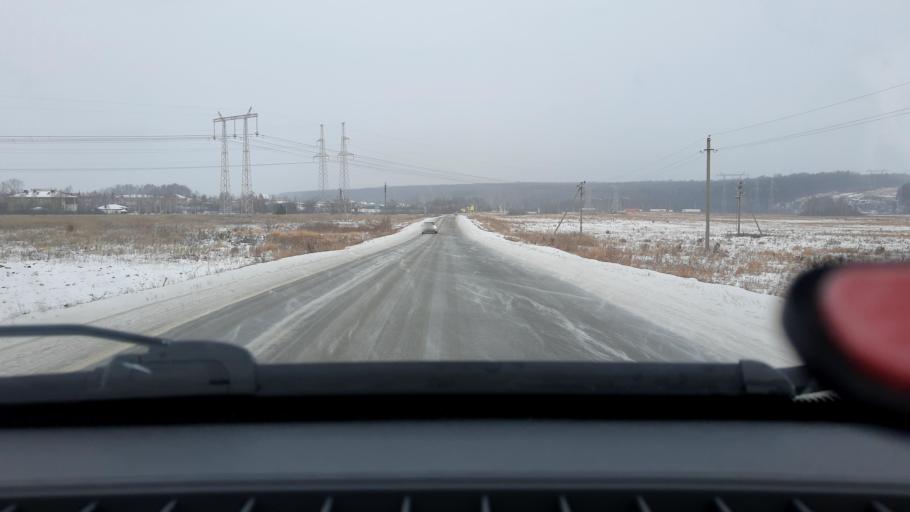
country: RU
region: Bashkortostan
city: Iglino
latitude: 54.7562
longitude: 56.3981
